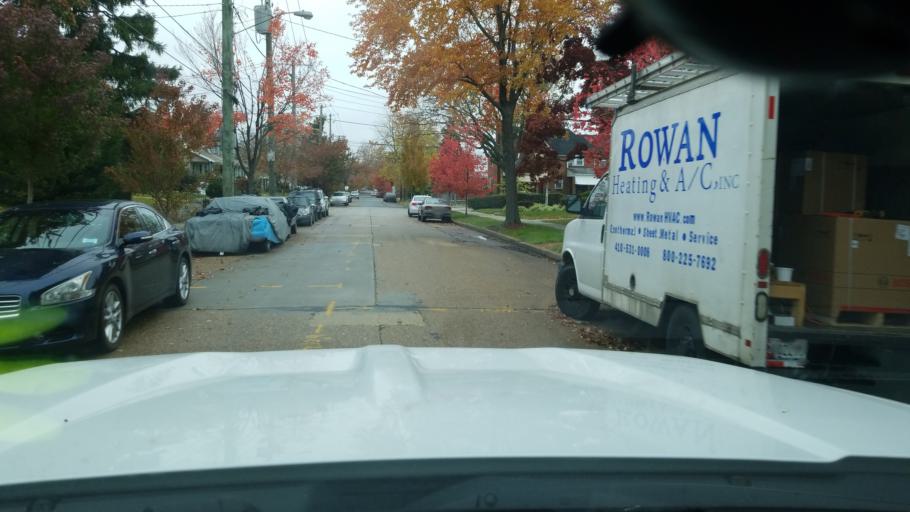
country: US
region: Maryland
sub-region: Prince George's County
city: Mount Rainier
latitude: 38.9390
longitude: -76.9762
